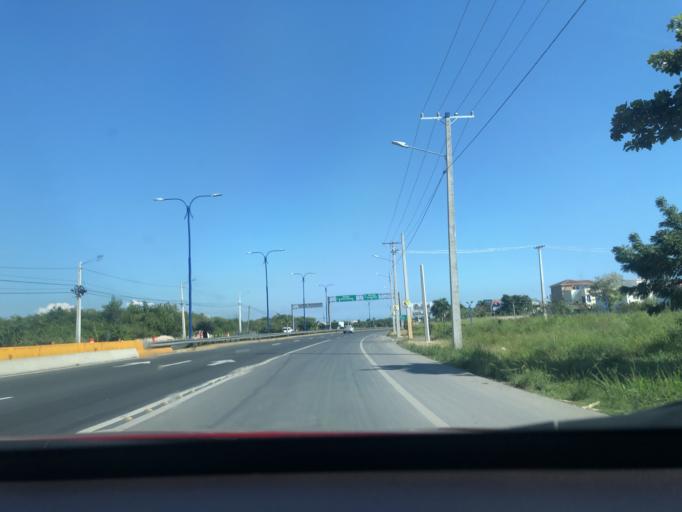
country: DO
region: Santo Domingo
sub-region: Santo Domingo
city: Boca Chica
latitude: 18.4542
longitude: -69.6023
